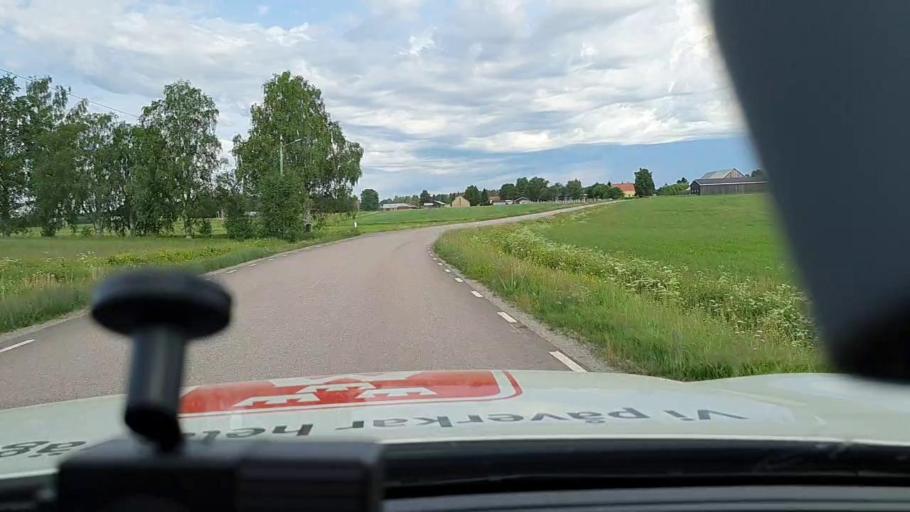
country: SE
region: Norrbotten
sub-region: Bodens Kommun
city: Saevast
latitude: 65.7061
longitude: 21.7634
